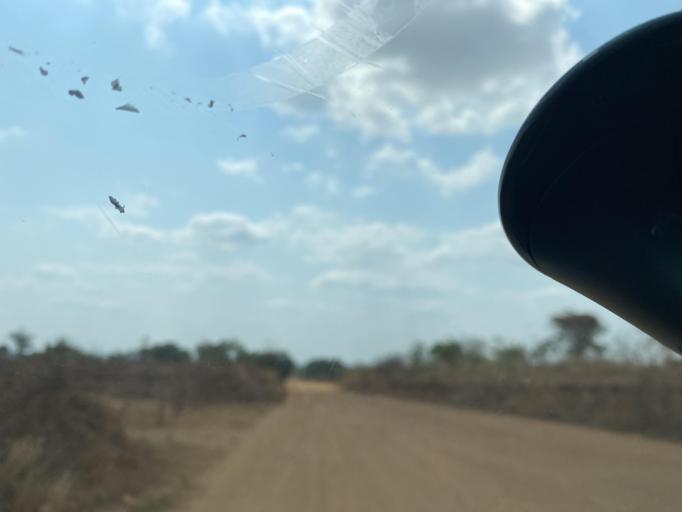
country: ZM
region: Lusaka
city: Chongwe
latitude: -15.5885
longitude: 28.7705
